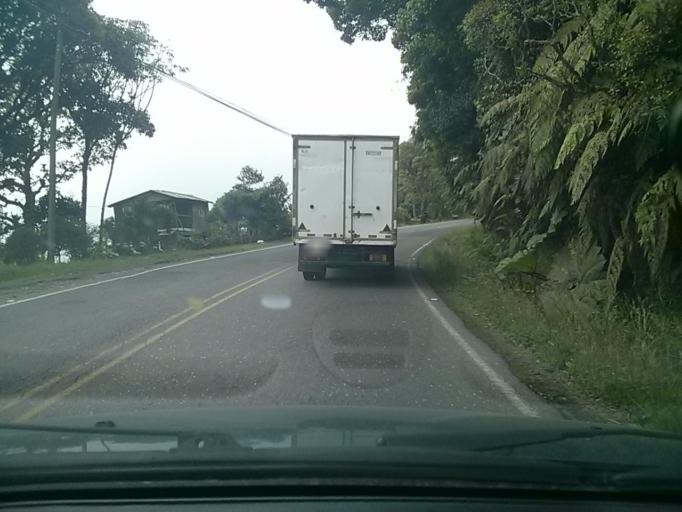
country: CR
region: Cartago
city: Tobosi
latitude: 9.7397
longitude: -83.9513
